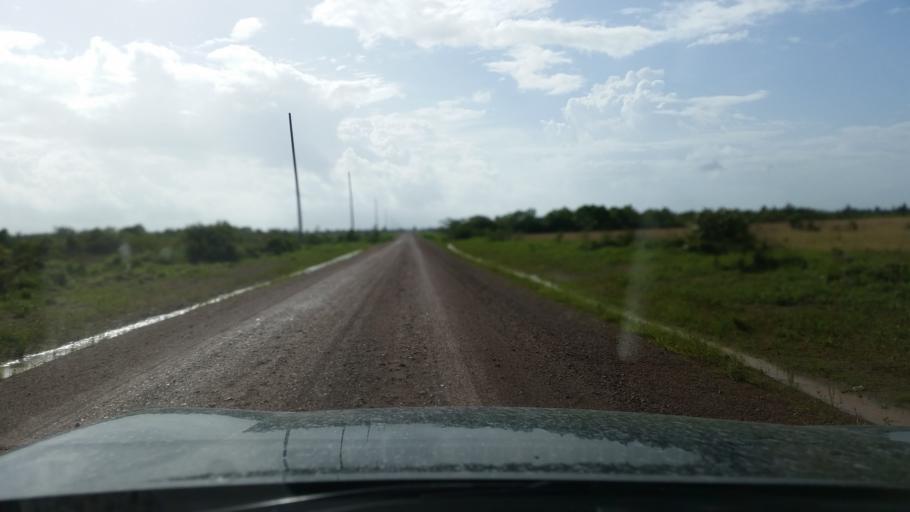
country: NI
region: Atlantico Norte (RAAN)
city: Puerto Cabezas
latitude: 14.1092
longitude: -83.5856
